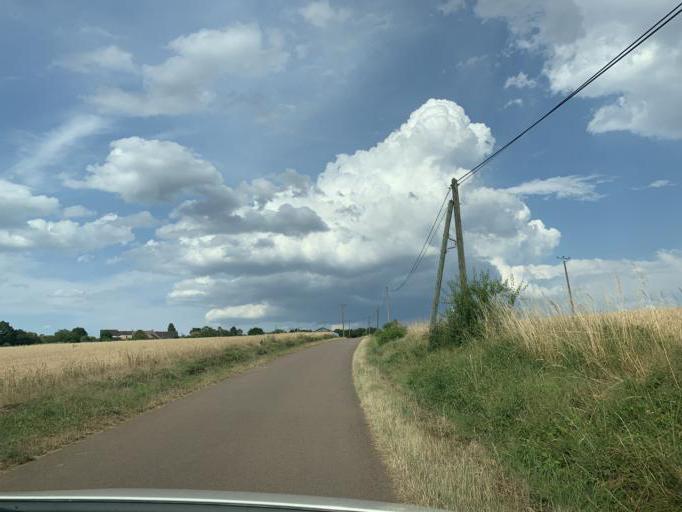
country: FR
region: Bourgogne
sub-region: Departement de l'Yonne
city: Fontenailles
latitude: 47.4940
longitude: 3.4271
